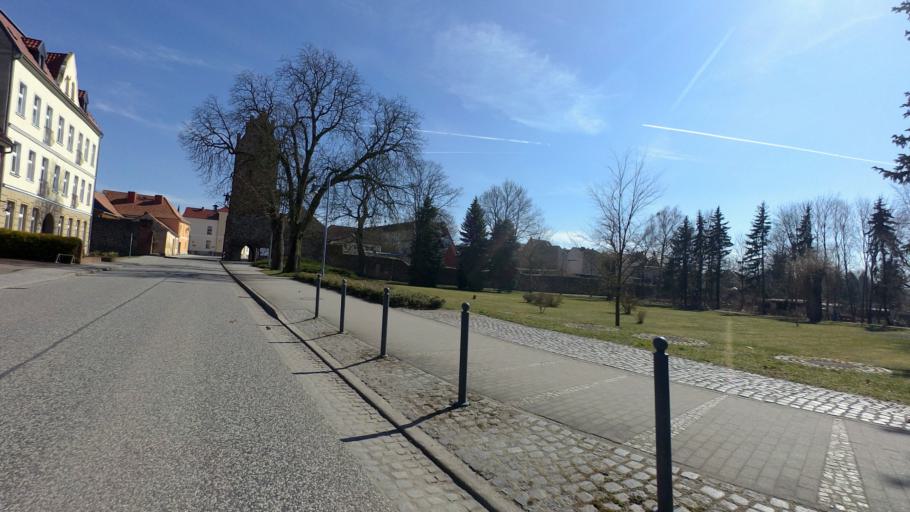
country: DE
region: Brandenburg
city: Muncheberg
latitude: 52.5052
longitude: 14.1373
